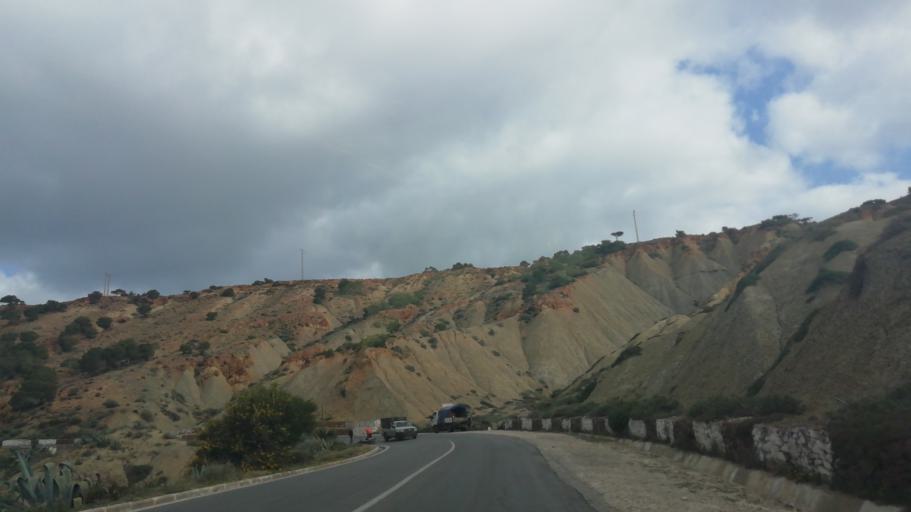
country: DZ
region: Relizane
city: Mazouna
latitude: 36.3064
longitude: 0.6711
